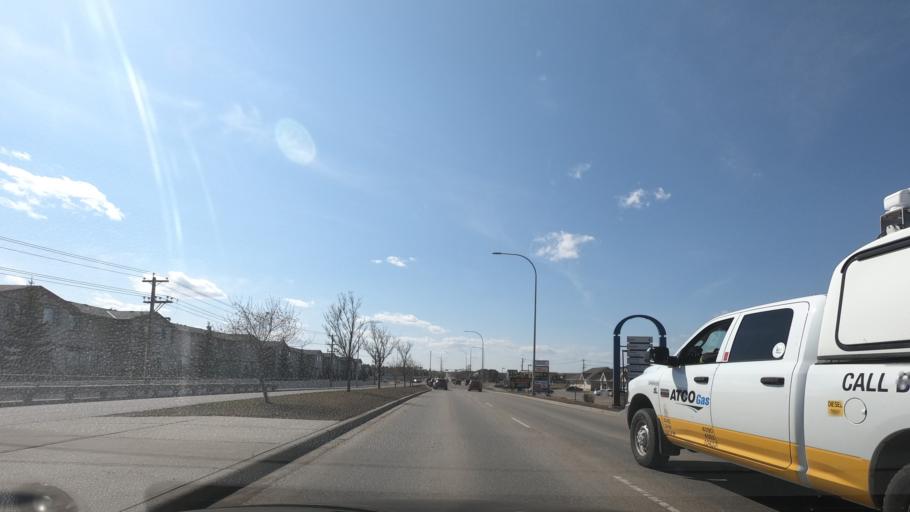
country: CA
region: Alberta
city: Airdrie
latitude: 51.3001
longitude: -114.0224
